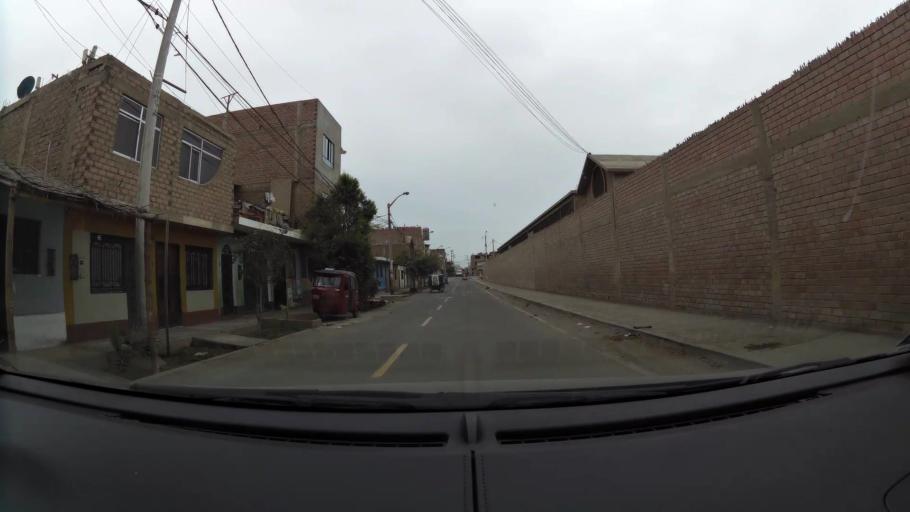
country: PE
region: Lima
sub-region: Barranca
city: Barranca
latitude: -10.7452
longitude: -77.7515
